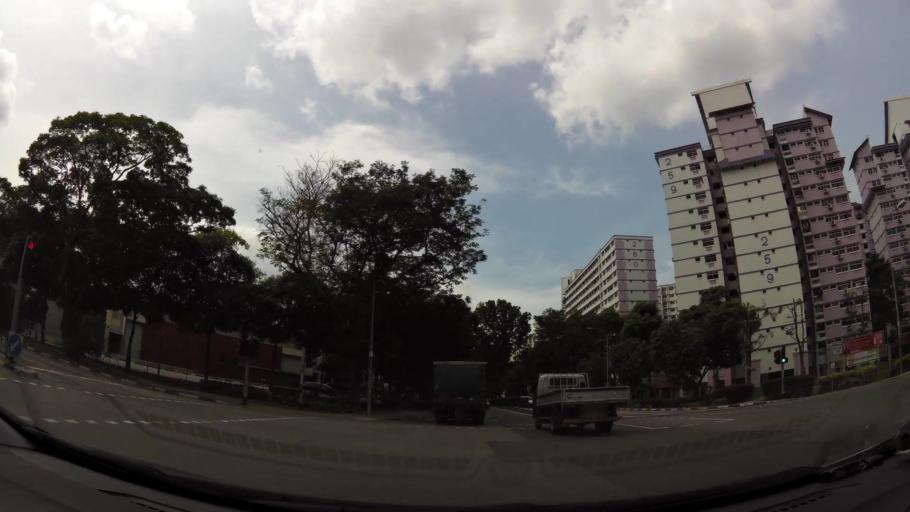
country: MY
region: Johor
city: Johor Bahru
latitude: 1.3455
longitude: 103.7094
